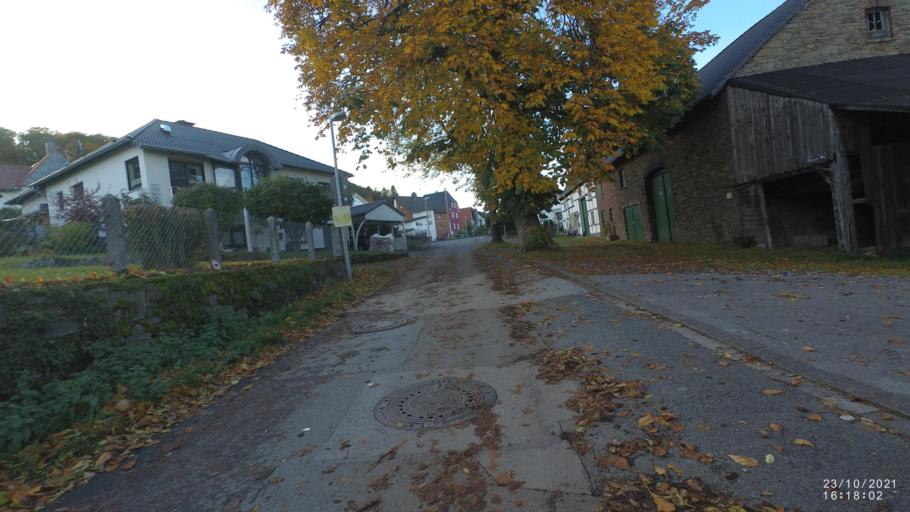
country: DE
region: North Rhine-Westphalia
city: Balve
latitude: 51.3751
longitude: 7.8345
